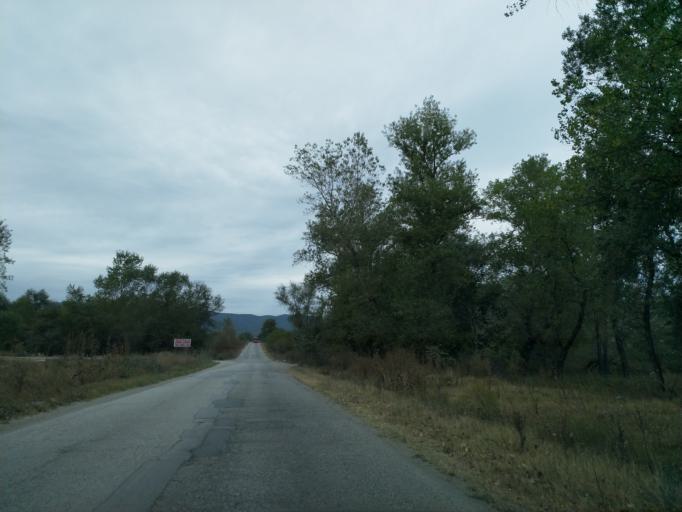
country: RS
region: Central Serbia
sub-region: Pomoravski Okrug
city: Paracin
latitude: 43.8268
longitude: 21.3500
